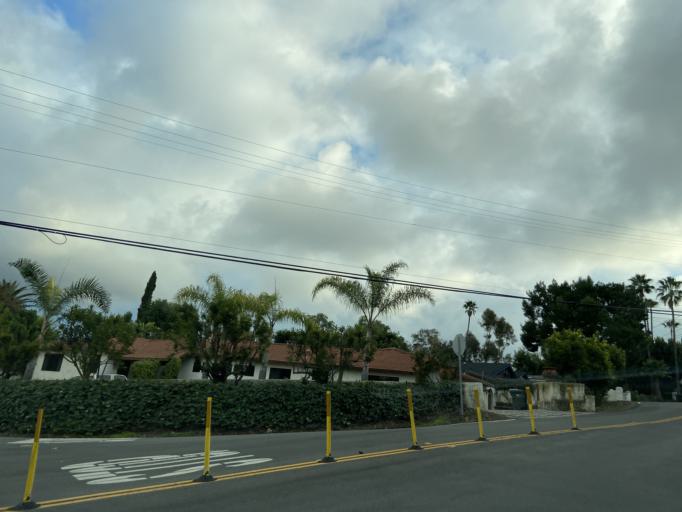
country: US
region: California
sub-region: San Diego County
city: Casa de Oro-Mount Helix
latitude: 32.7651
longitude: -116.9649
